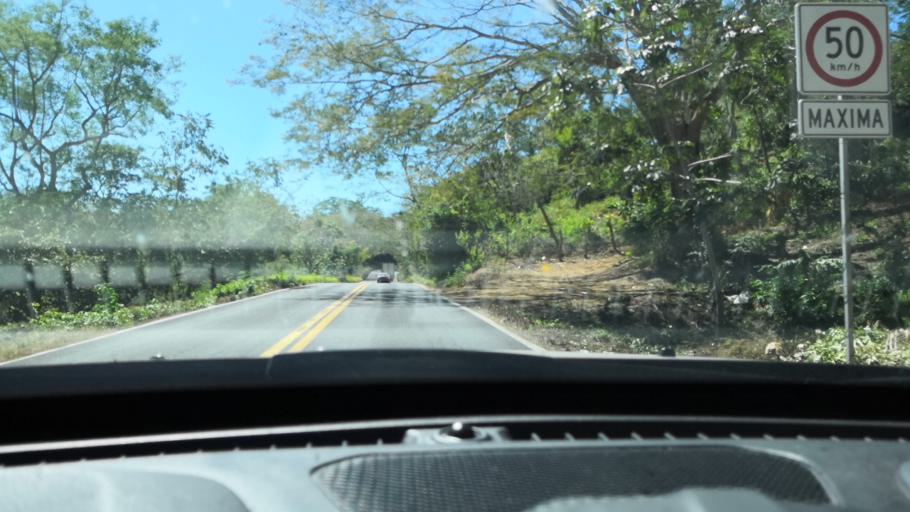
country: MX
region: Nayarit
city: Compostela
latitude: 21.2149
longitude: -104.9861
